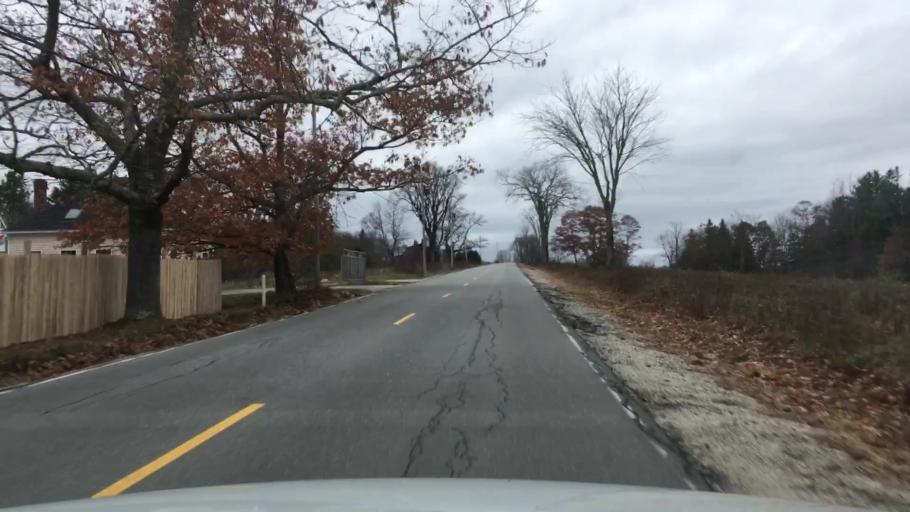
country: US
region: Maine
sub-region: Hancock County
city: Penobscot
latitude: 44.4377
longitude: -68.6334
